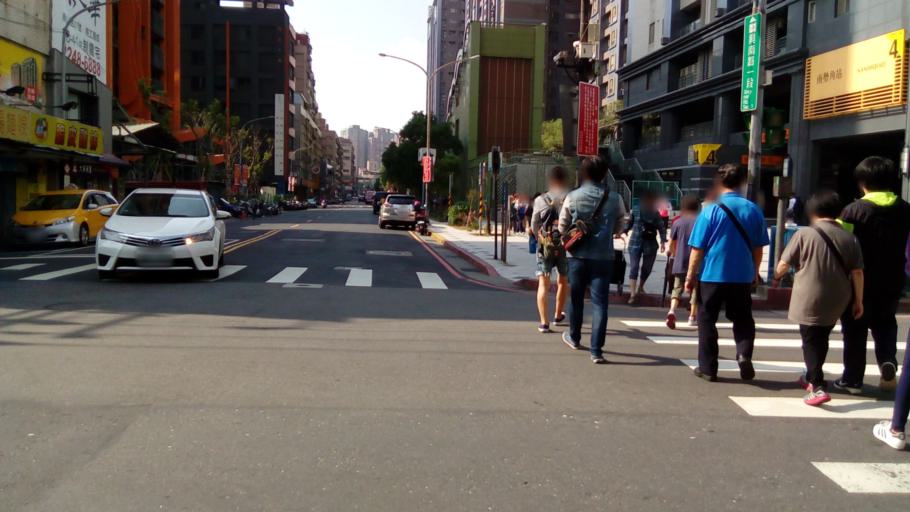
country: TW
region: Taipei
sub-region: Taipei
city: Banqiao
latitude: 24.9894
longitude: 121.5100
